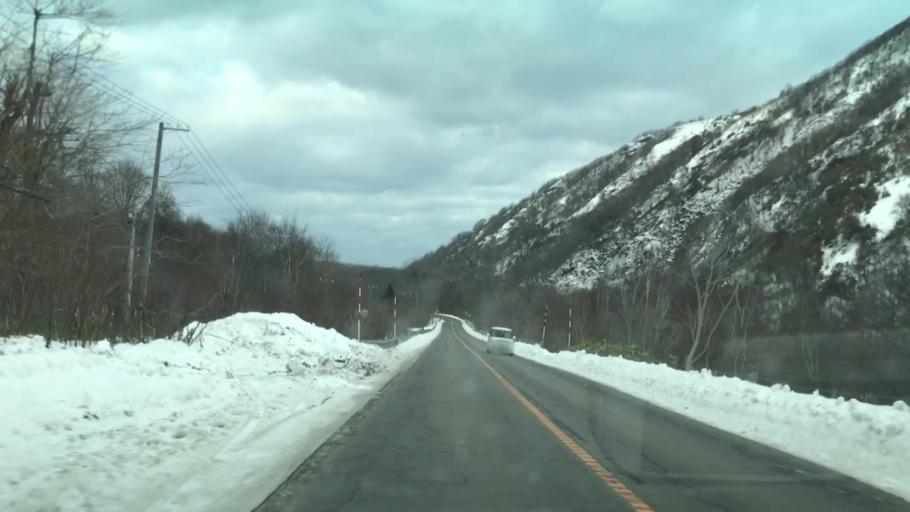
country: JP
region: Hokkaido
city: Yoichi
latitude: 43.3300
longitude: 140.4798
